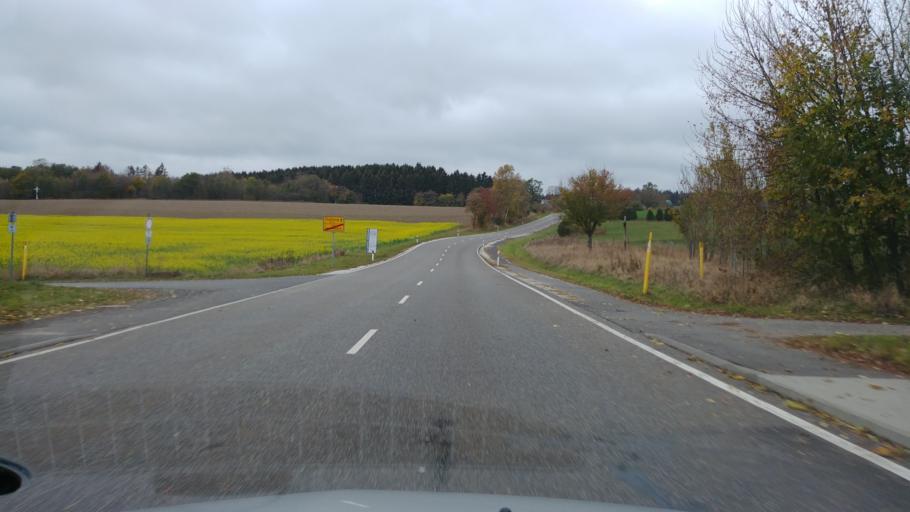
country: DE
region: Rheinland-Pfalz
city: Hermeskeil
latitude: 49.6642
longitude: 6.9486
